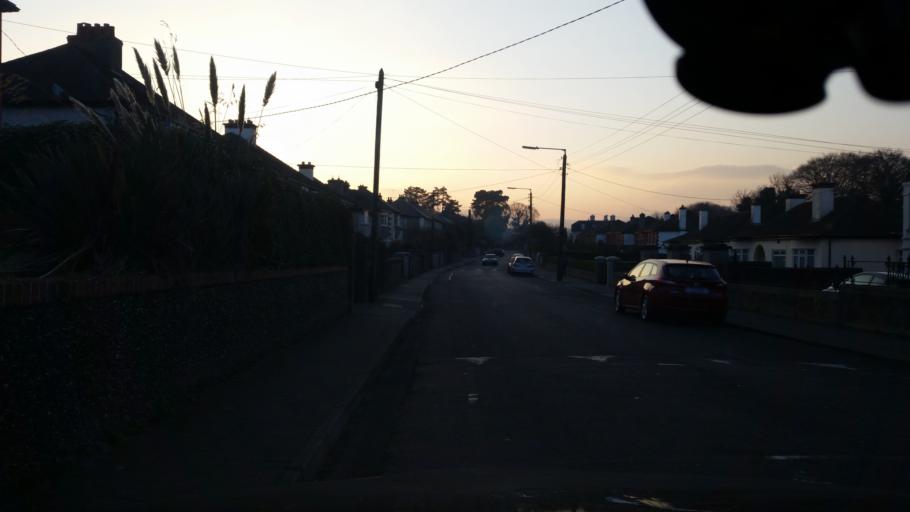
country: IE
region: Leinster
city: Little Bray
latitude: 53.2034
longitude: -6.1133
